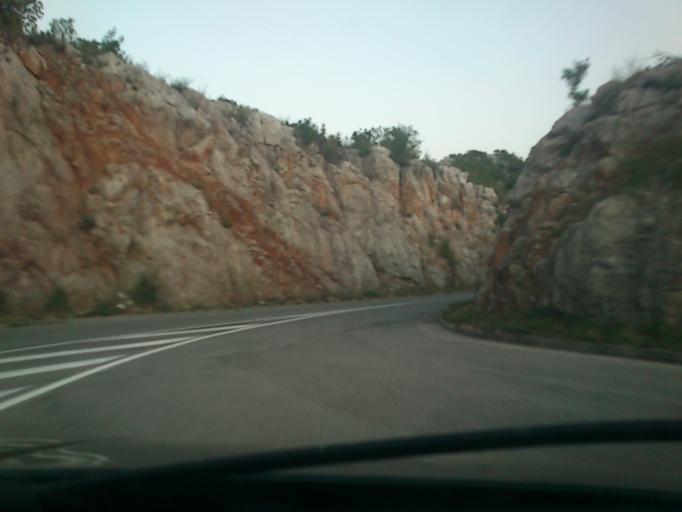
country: HR
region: Licko-Senjska
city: Senj
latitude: 44.9244
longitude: 14.9172
